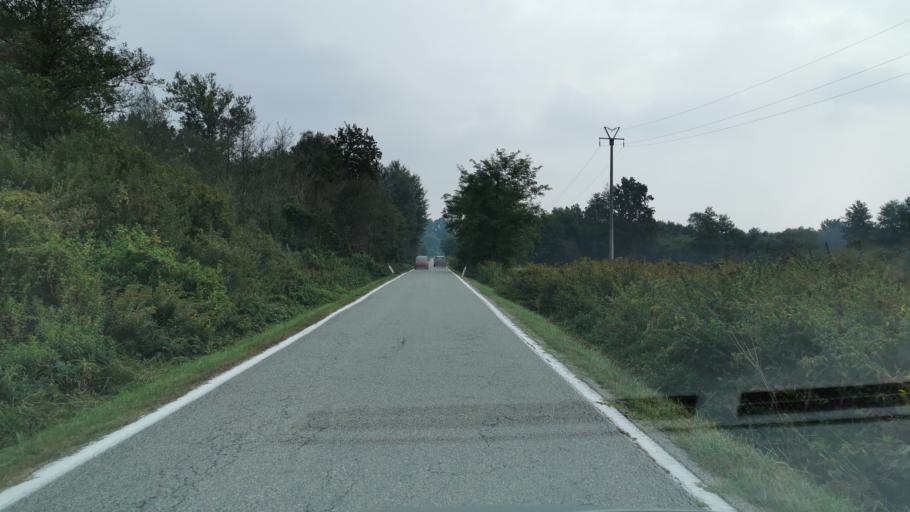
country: IT
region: Piedmont
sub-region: Provincia di Torino
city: Montanaro
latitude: 45.2487
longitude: 7.8331
